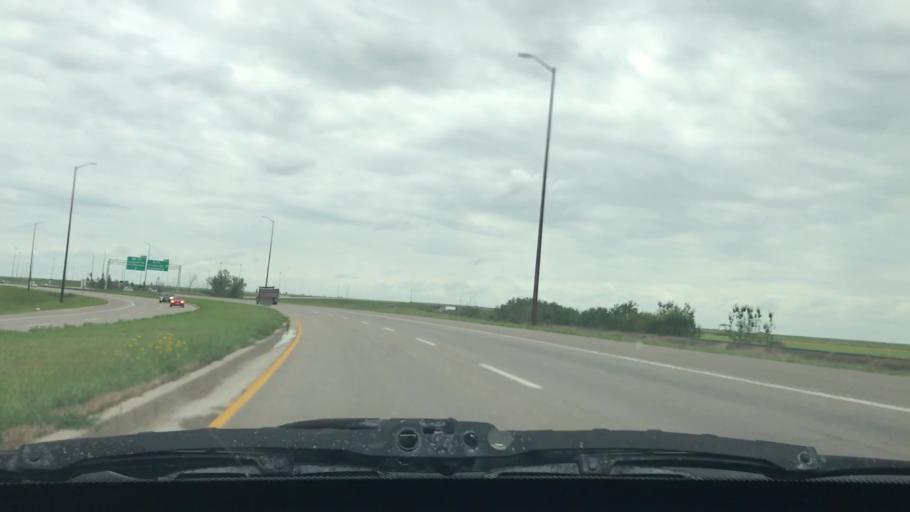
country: CA
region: Manitoba
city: Winnipeg
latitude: 49.8366
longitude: -96.9757
